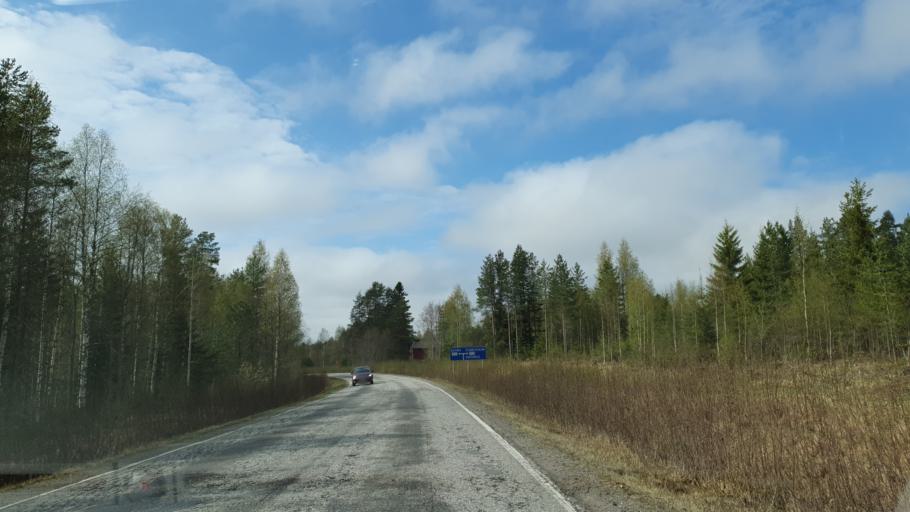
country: FI
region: Kainuu
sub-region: Kehys-Kainuu
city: Kuhmo
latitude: 64.1287
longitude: 29.5939
